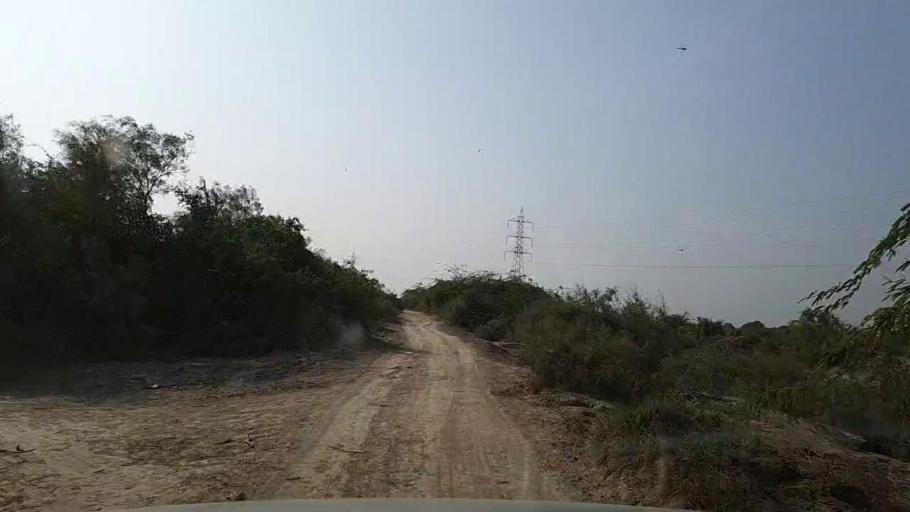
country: PK
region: Sindh
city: Mirpur Sakro
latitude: 24.5754
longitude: 67.5806
